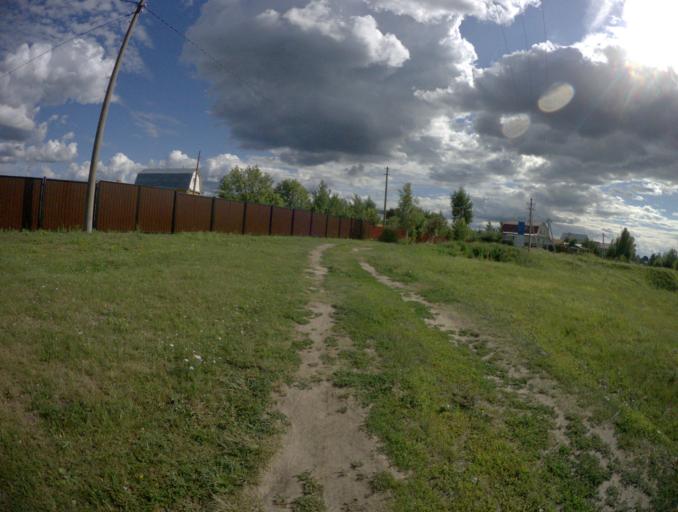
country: RU
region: Vladimir
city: Kideksha
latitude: 56.3296
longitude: 40.5948
